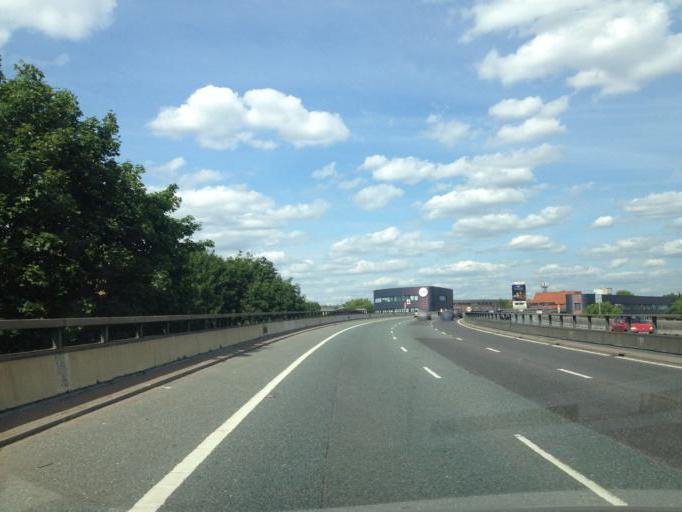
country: GB
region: England
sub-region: Greater London
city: Bayswater
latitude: 51.5203
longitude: -0.2052
